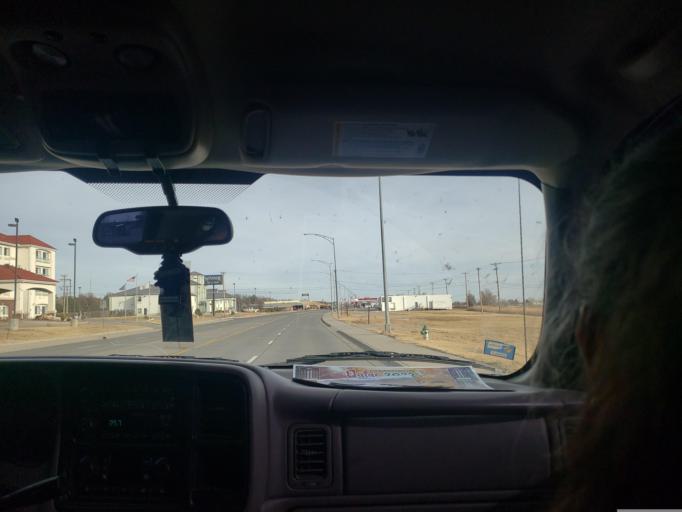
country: US
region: Kansas
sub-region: Ford County
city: Dodge City
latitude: 37.7543
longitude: -100.0482
